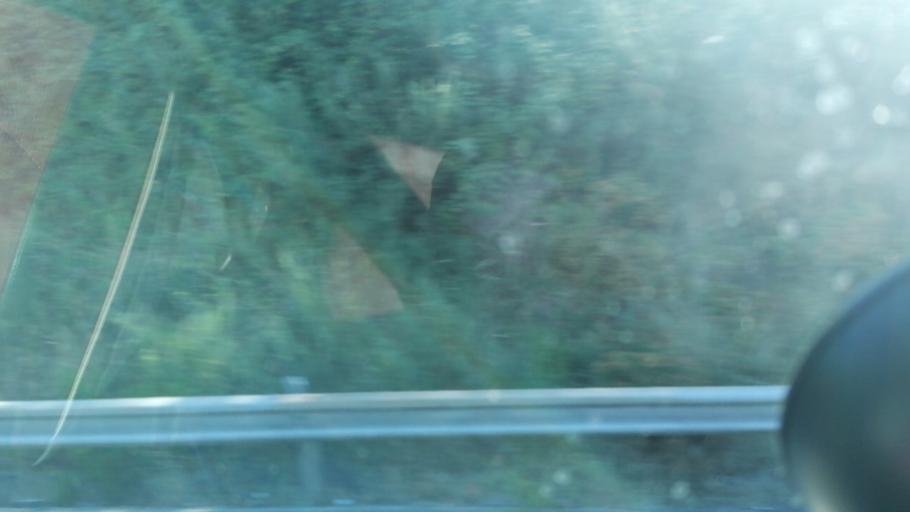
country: PT
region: Porto
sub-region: Santo Tirso
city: Santo Tirso
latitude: 41.3391
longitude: -8.5042
